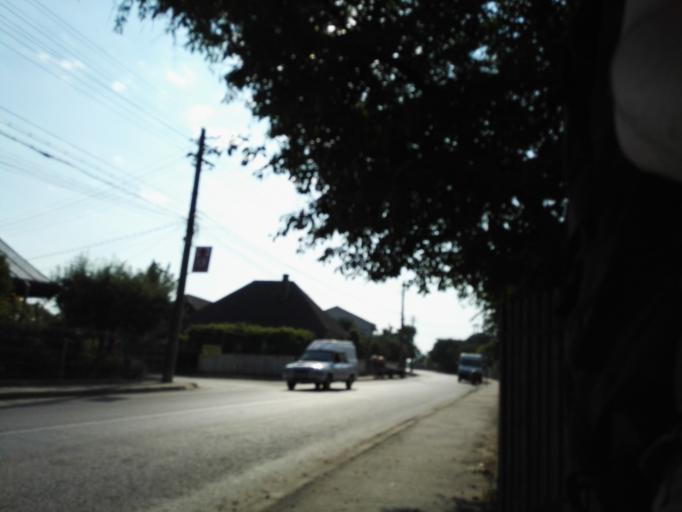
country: RO
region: Suceava
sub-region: Comuna Radaseni
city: Radaseni
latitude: 47.4684
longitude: 26.2755
